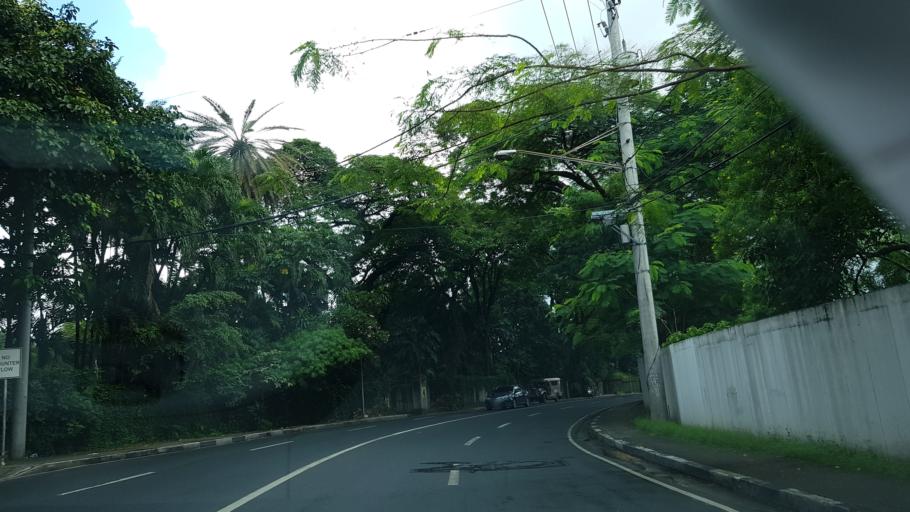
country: PH
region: Metro Manila
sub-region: Makati City
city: Makati City
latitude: 14.5449
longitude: 121.0444
